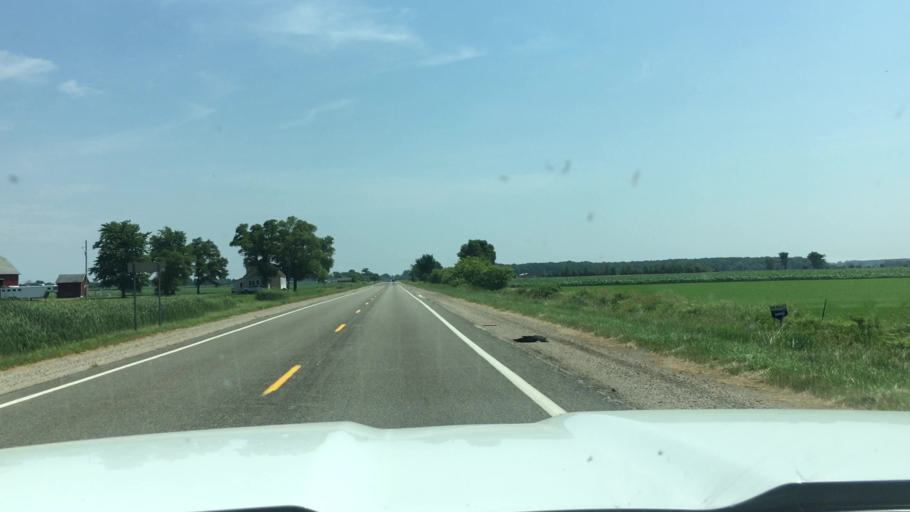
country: US
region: Michigan
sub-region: Gratiot County
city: Ithaca
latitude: 43.1758
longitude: -84.5212
